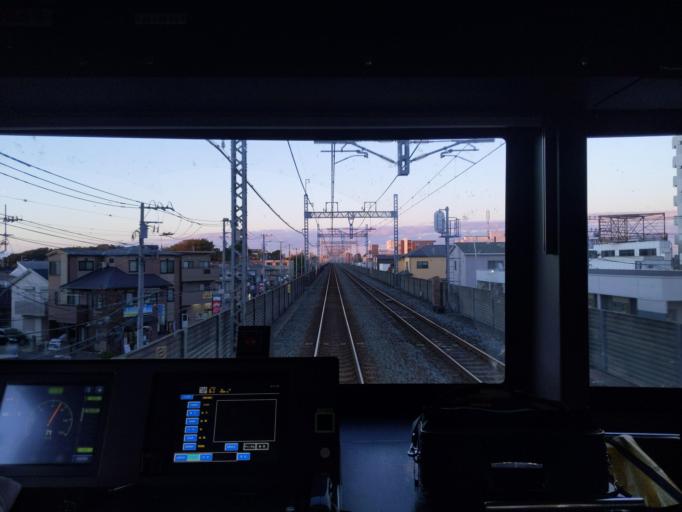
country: JP
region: Chiba
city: Funabashi
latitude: 35.7656
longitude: 139.9976
